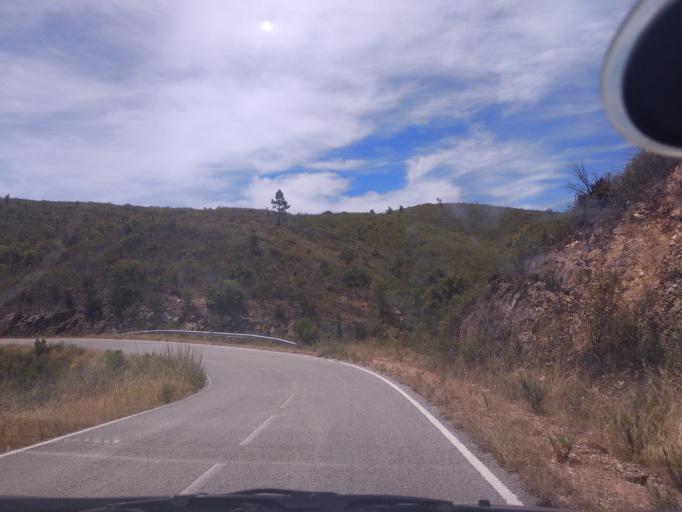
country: PT
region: Faro
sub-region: Sao Bras de Alportel
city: Sao Bras de Alportel
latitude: 37.2032
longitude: -7.8099
